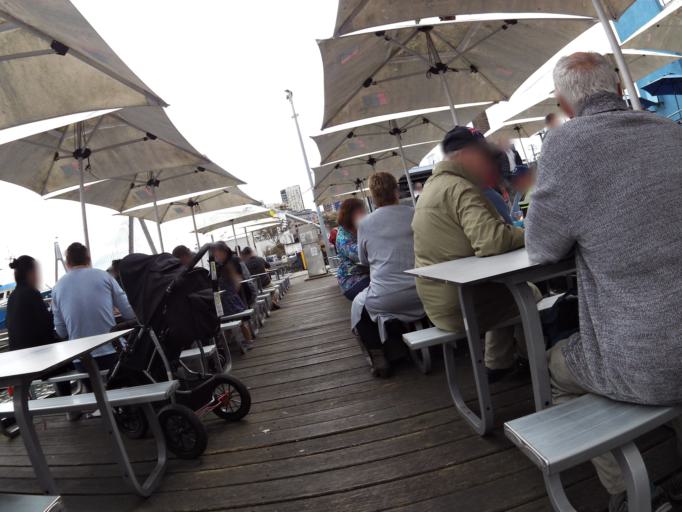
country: AU
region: New South Wales
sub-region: City of Sydney
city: Haberfield
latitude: -33.8729
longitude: 151.1917
